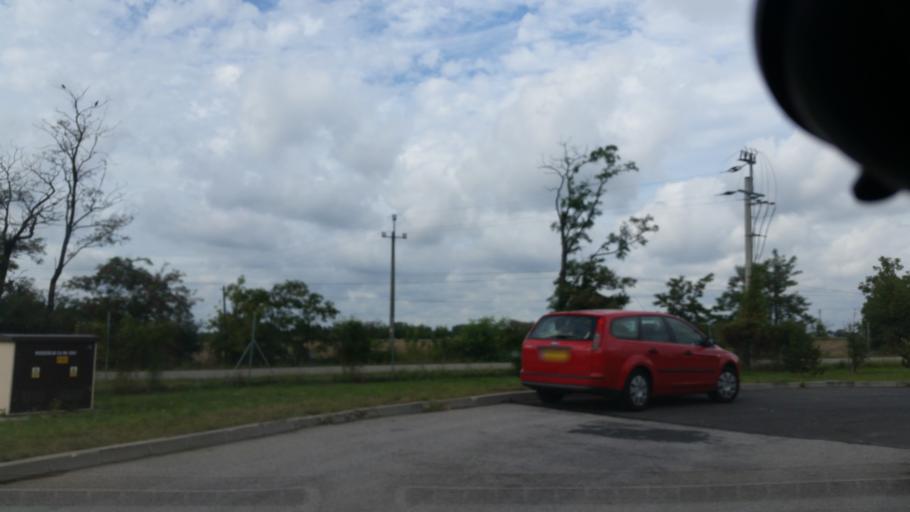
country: PL
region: Masovian Voivodeship
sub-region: Powiat pruszkowski
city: Brwinow
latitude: 52.1559
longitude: 20.6839
